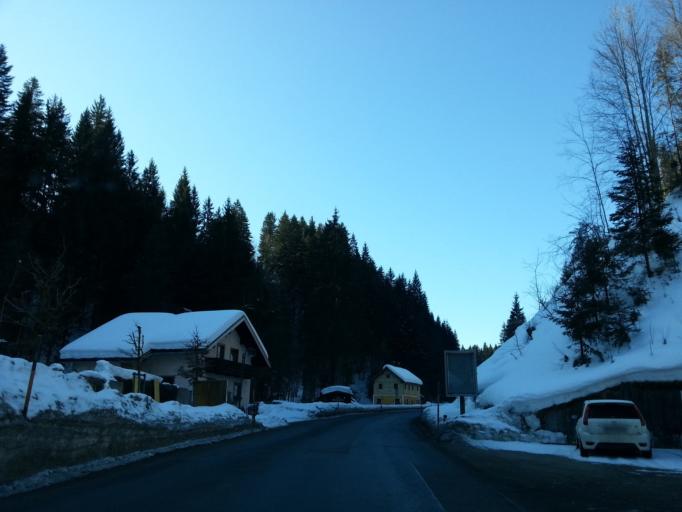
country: AT
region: Salzburg
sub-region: Politischer Bezirk Hallein
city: Abtenau
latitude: 47.4934
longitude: 13.3989
